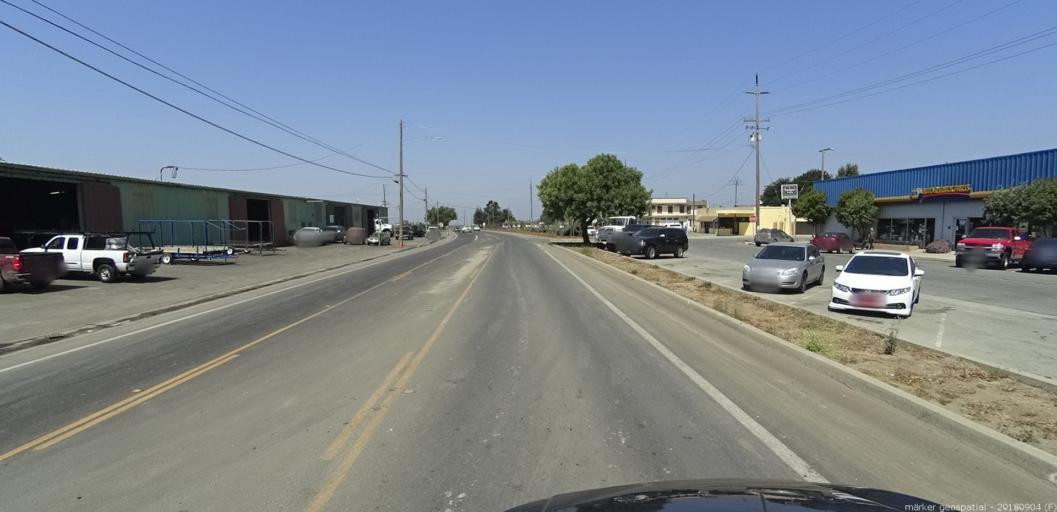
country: US
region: California
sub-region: Monterey County
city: Gonzales
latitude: 36.5091
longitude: -121.4479
